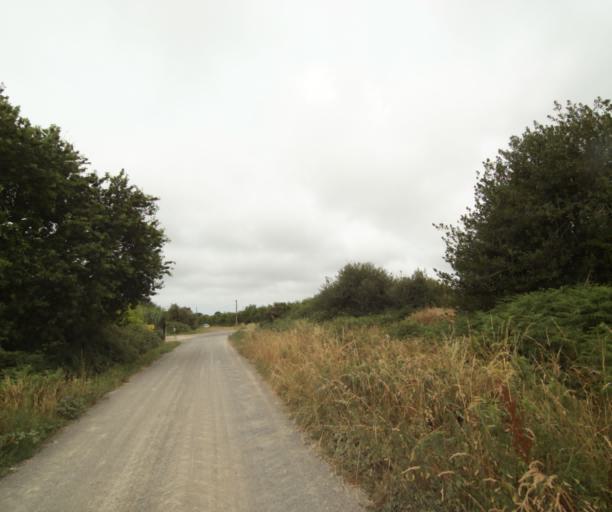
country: FR
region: Pays de la Loire
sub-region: Departement de la Vendee
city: Sainte-Foy
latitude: 46.5094
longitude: -1.6856
